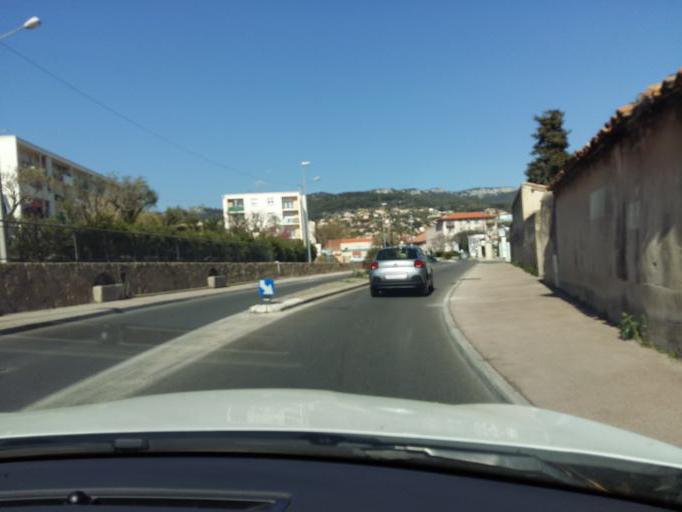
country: FR
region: Provence-Alpes-Cote d'Azur
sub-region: Departement du Var
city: Ollioules
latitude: 43.1316
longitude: 5.8445
